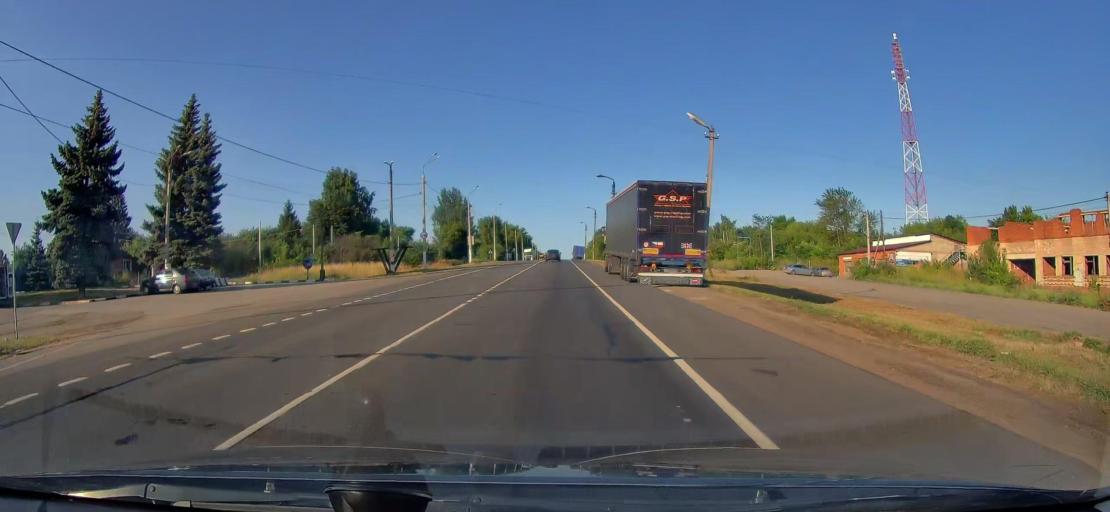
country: RU
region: Tula
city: Plavsk
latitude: 53.6967
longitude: 37.2806
